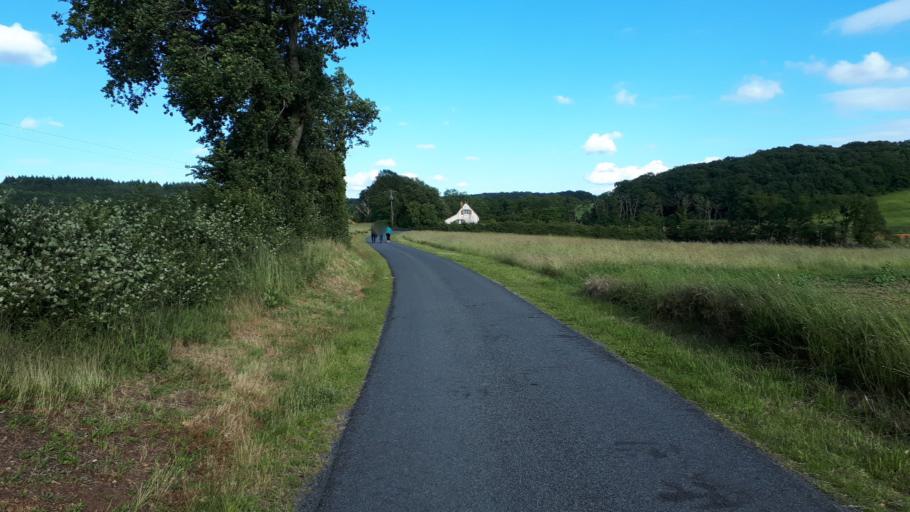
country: FR
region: Centre
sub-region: Departement du Loir-et-Cher
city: Sarge-sur-Braye
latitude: 47.9270
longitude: 0.8650
